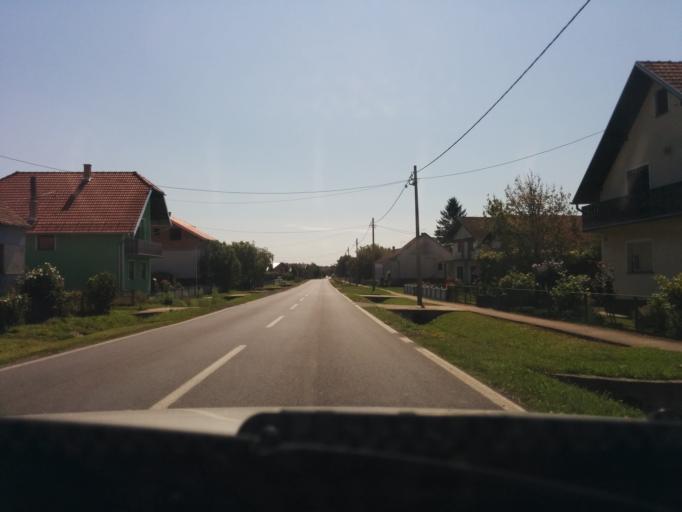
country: HR
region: Sisacko-Moslavacka
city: Lipovljani
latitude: 45.3703
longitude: 16.9248
